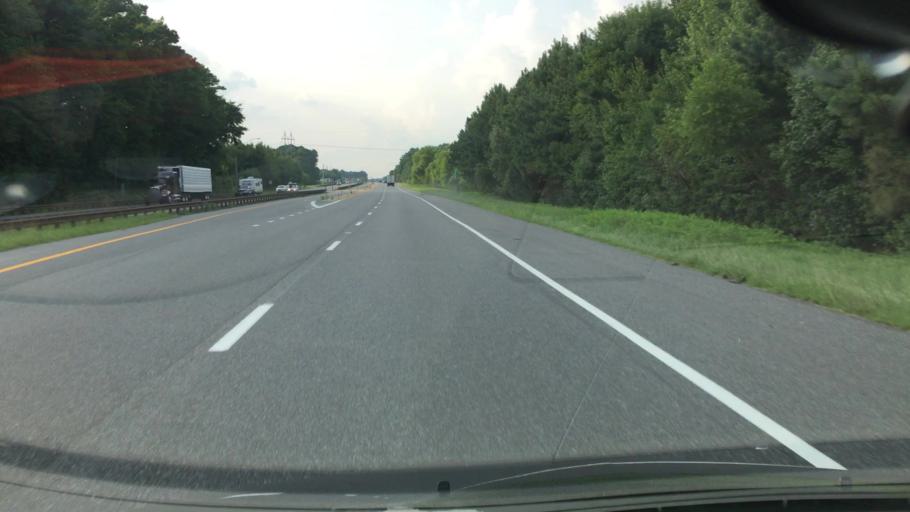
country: US
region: Delaware
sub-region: Sussex County
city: Selbyville
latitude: 38.4203
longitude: -75.2147
